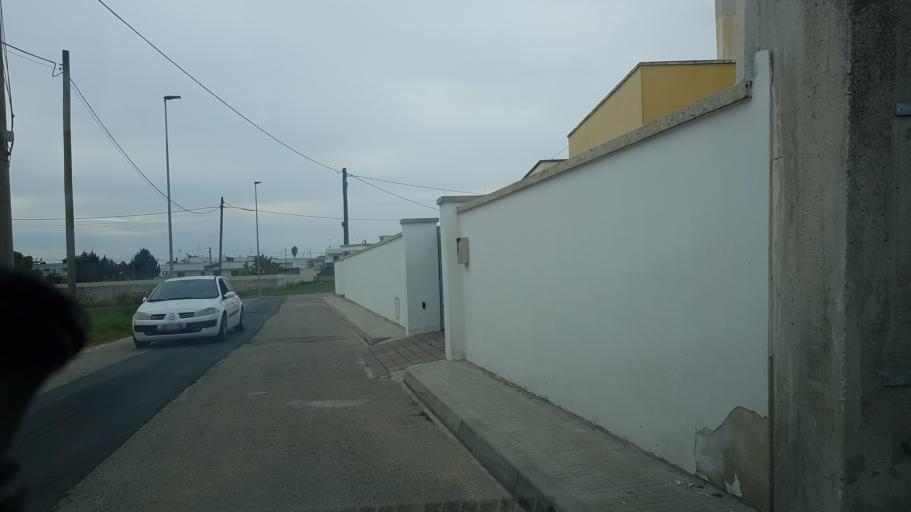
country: IT
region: Apulia
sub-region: Provincia di Lecce
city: Leverano
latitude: 40.2994
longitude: 17.9993
